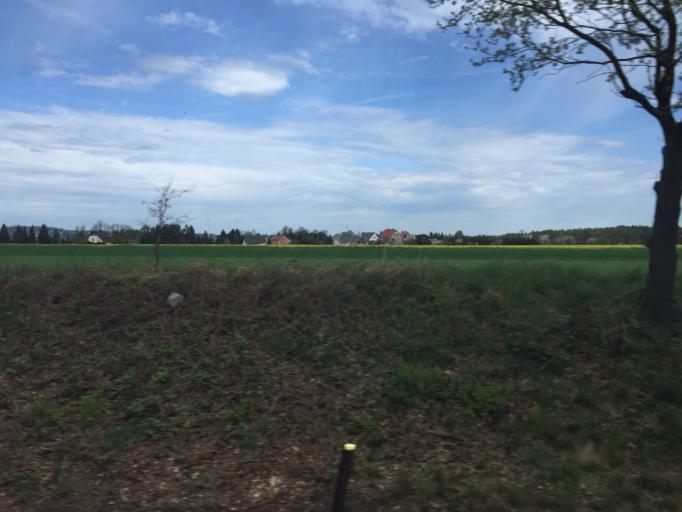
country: DE
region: Saxony
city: Demitz-Thumitz
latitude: 51.1430
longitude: 14.2856
